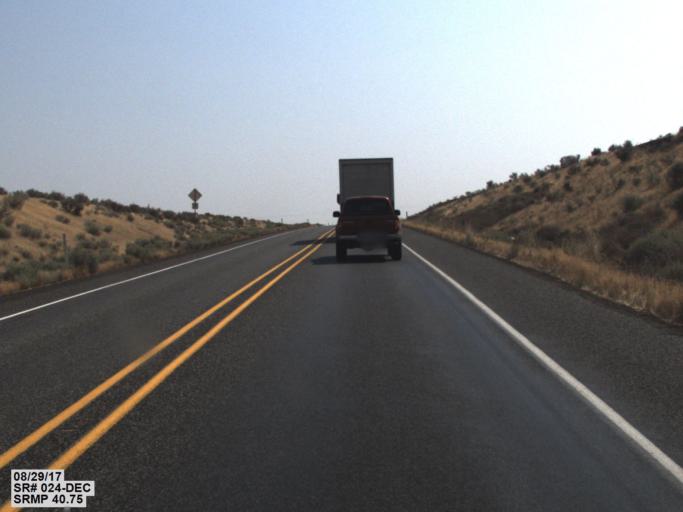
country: US
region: Washington
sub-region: Grant County
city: Desert Aire
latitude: 46.6050
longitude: -119.7326
